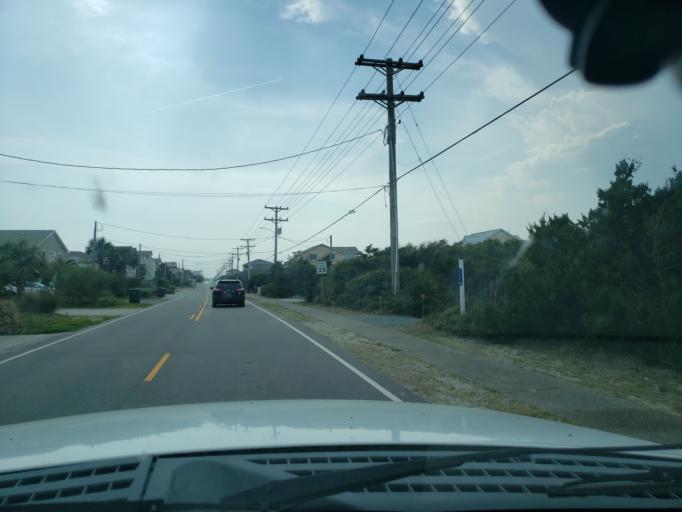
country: US
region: North Carolina
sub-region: Pender County
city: Surf City
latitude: 34.3831
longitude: -77.6068
